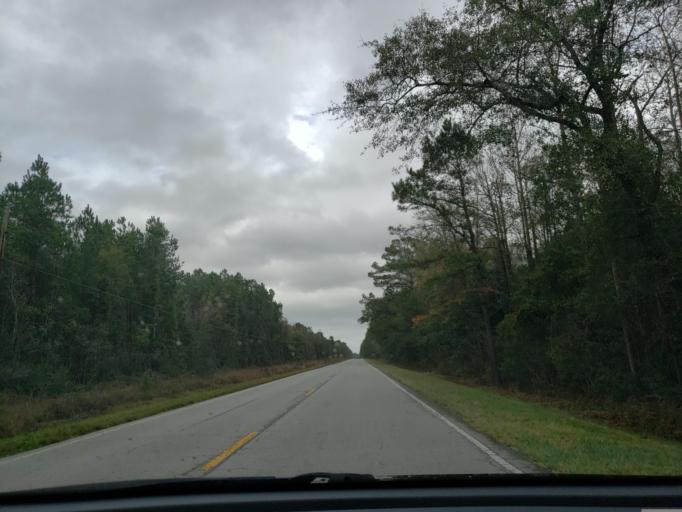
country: US
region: North Carolina
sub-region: Onslow County
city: Jacksonville
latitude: 34.7224
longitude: -77.6113
